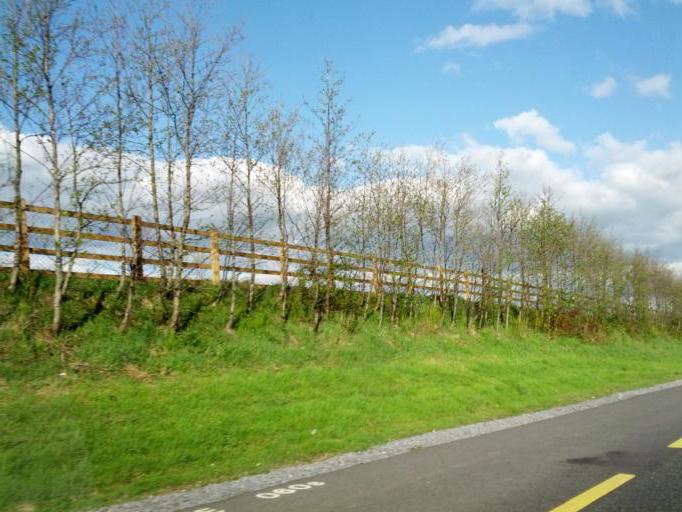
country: IE
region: Leinster
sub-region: An Iarmhi
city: Athlone
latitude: 53.4290
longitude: -7.9175
